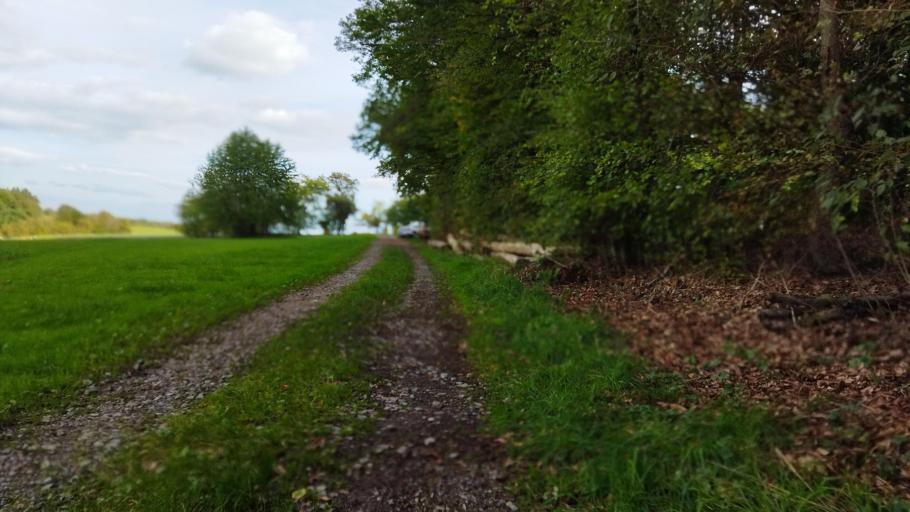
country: DE
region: Baden-Wuerttemberg
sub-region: Karlsruhe Region
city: Sternenfels
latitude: 49.0671
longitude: 8.8791
